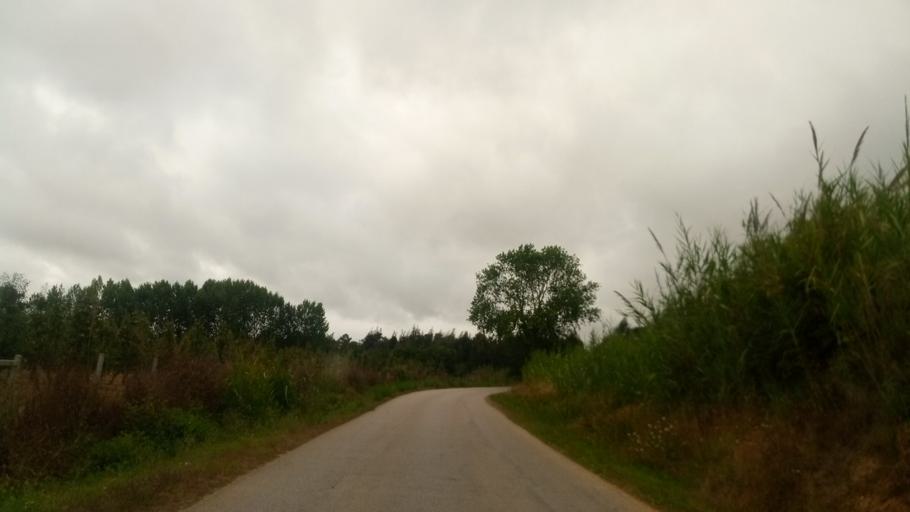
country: PT
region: Leiria
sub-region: Caldas da Rainha
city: Caldas da Rainha
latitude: 39.4245
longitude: -9.1408
